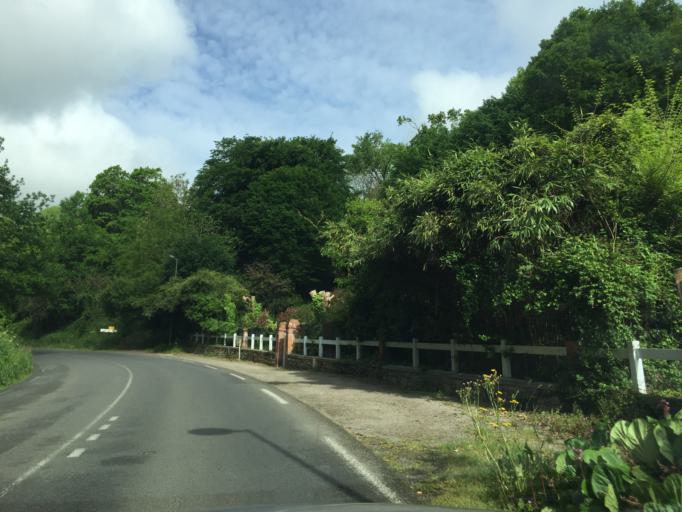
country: FR
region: Brittany
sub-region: Departement des Cotes-d'Armor
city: Matignon
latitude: 48.6206
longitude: -2.3414
